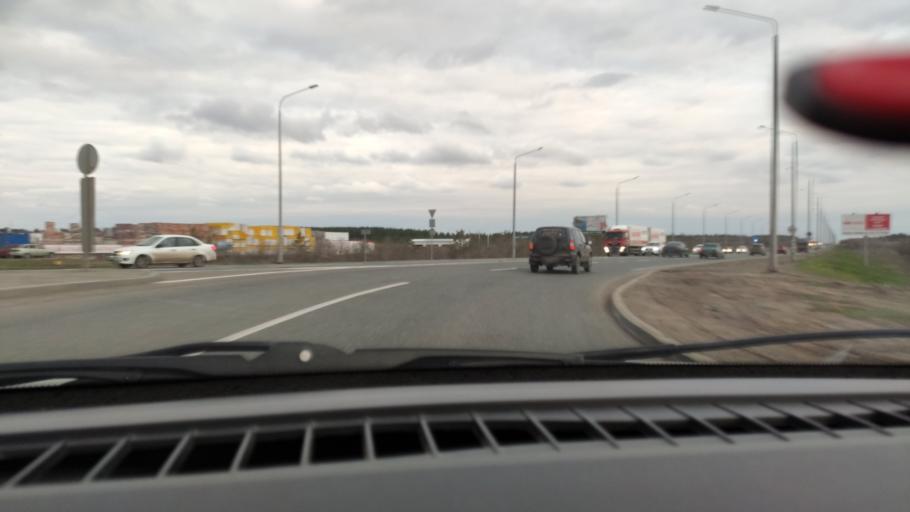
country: RU
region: Orenburg
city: Prigorodnyy
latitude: 51.8115
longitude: 55.1847
